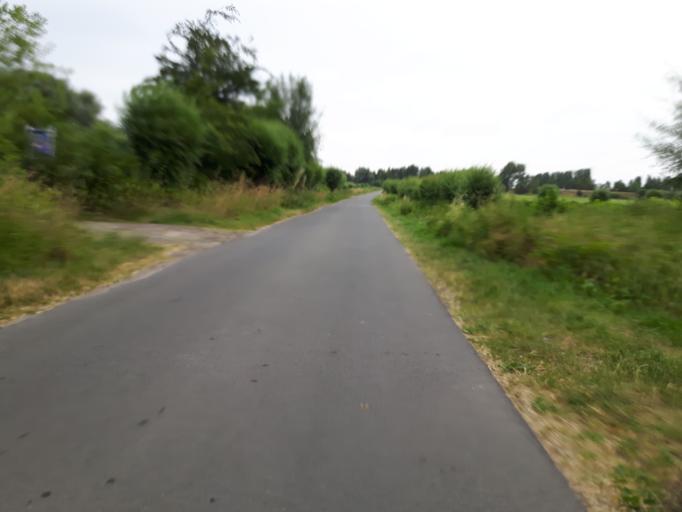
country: DE
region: Lower Saxony
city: Stelle
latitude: 53.3927
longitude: 10.0994
